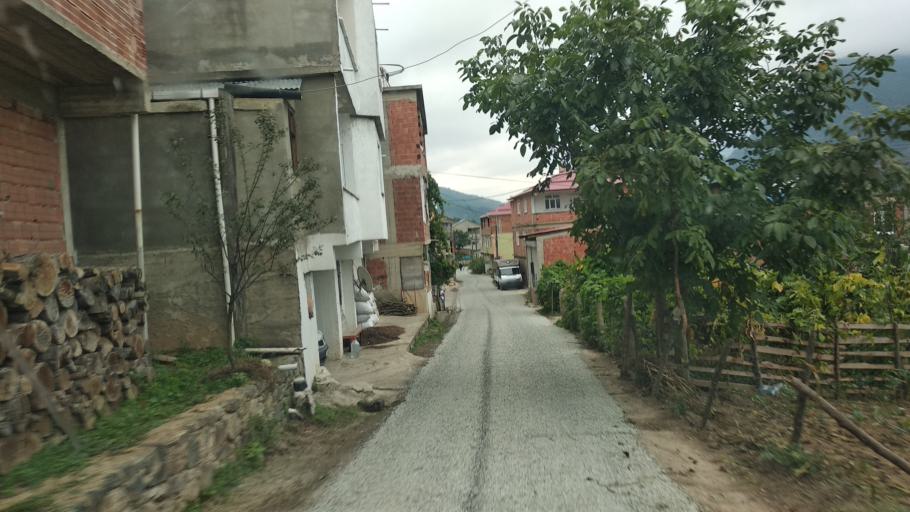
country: TR
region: Giresun
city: Dogankent
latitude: 40.7477
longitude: 38.9857
